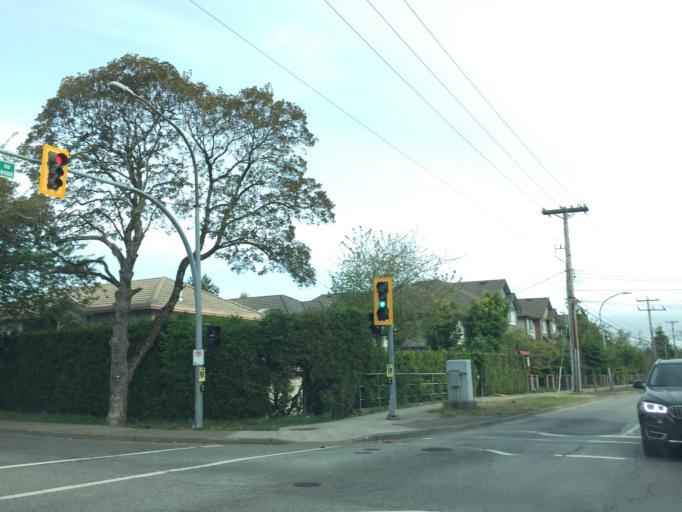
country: CA
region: British Columbia
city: Richmond
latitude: 49.1410
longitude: -123.1589
